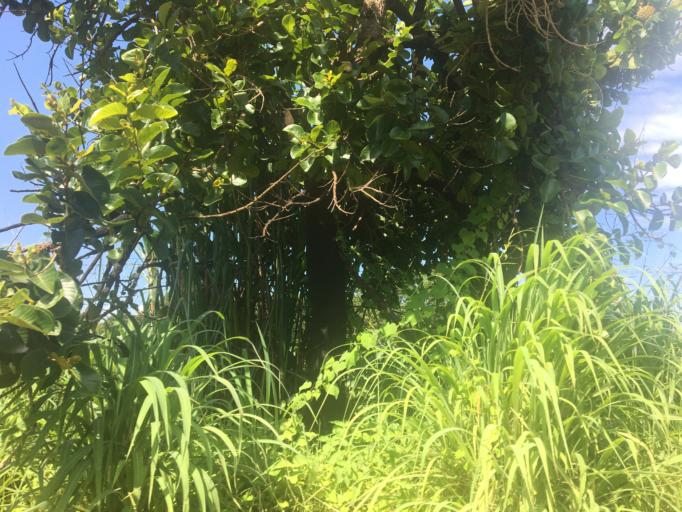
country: BR
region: Federal District
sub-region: Brasilia
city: Brasilia
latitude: -15.9649
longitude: -48.1318
